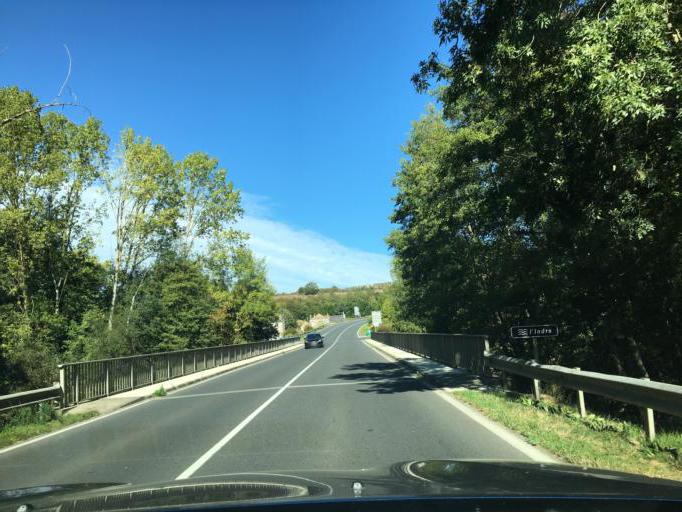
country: FR
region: Centre
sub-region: Departement d'Indre-et-Loire
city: Azay-le-Rideau
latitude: 47.2606
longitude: 0.4575
